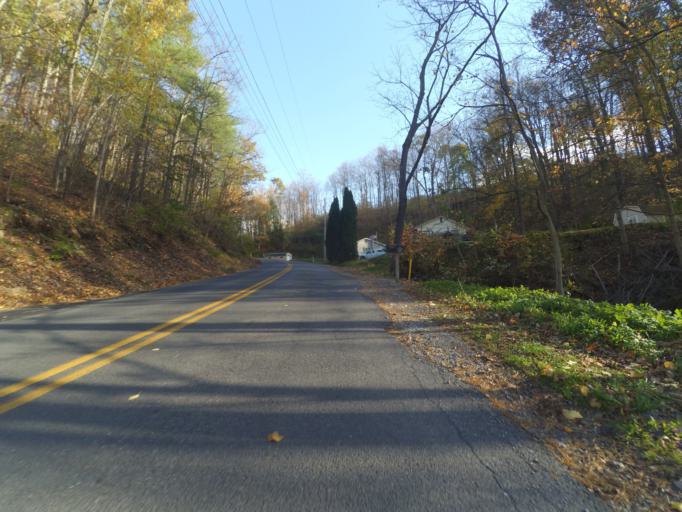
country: US
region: Pennsylvania
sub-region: Centre County
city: Bellefonte
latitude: 40.8820
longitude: -77.7857
